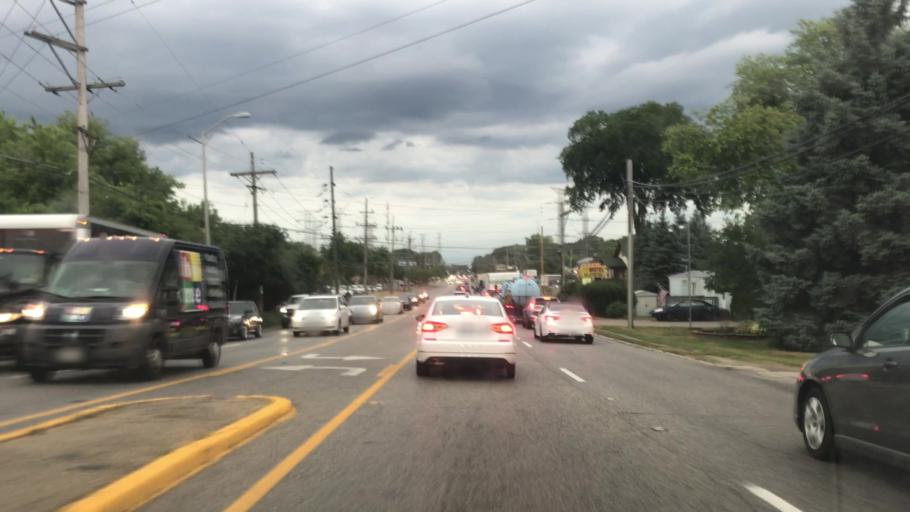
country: US
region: Illinois
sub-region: Cook County
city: Des Plaines
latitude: 42.0499
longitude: -87.8901
